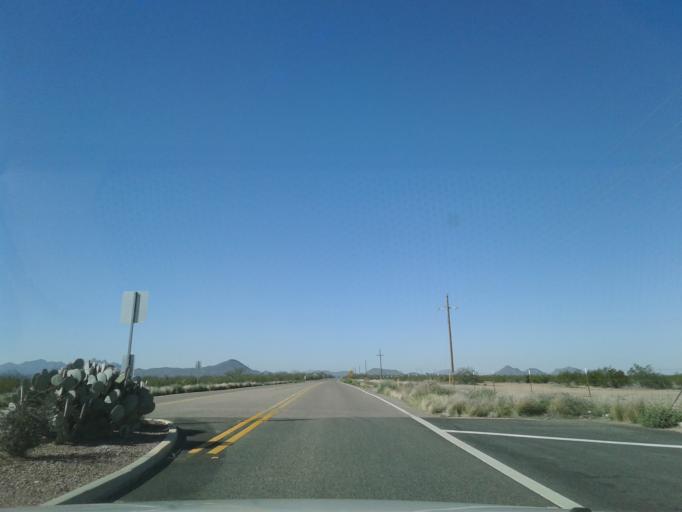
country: US
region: Arizona
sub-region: Pima County
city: Avra Valley
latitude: 32.5671
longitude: -111.3458
